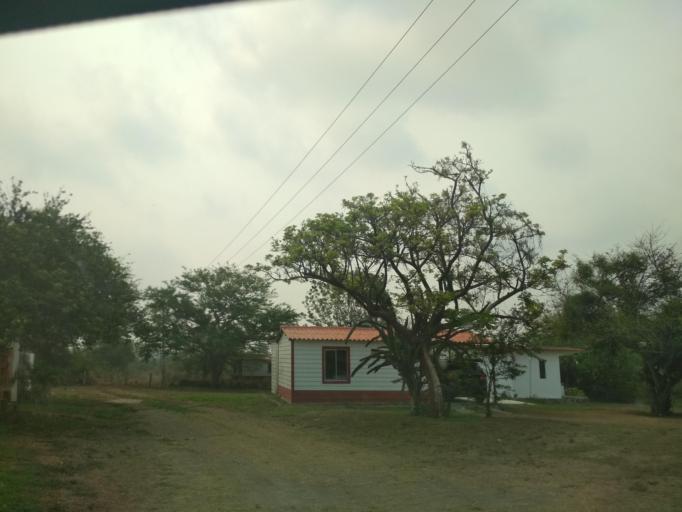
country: MX
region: Veracruz
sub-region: Veracruz
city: Fraccionamiento Geovillas los Pinos
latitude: 19.2102
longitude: -96.2467
